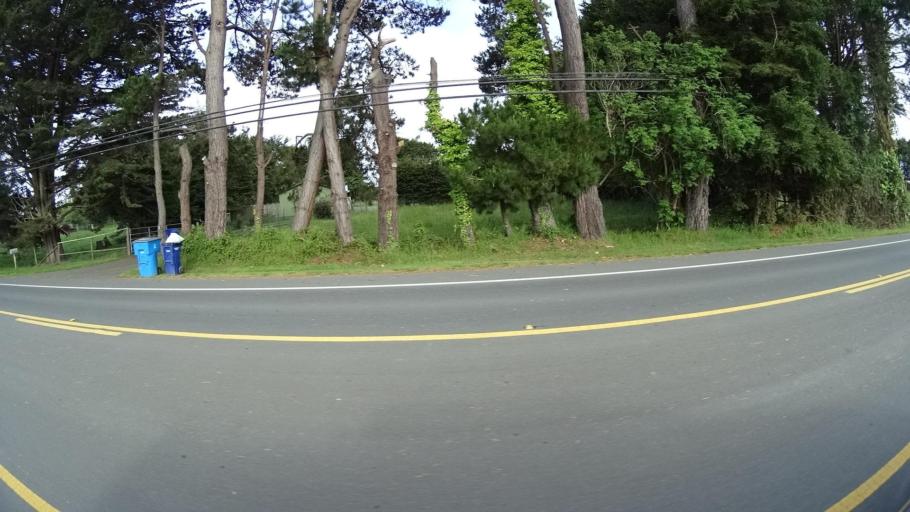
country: US
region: California
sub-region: Humboldt County
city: Arcata
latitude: 40.8997
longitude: -124.0918
